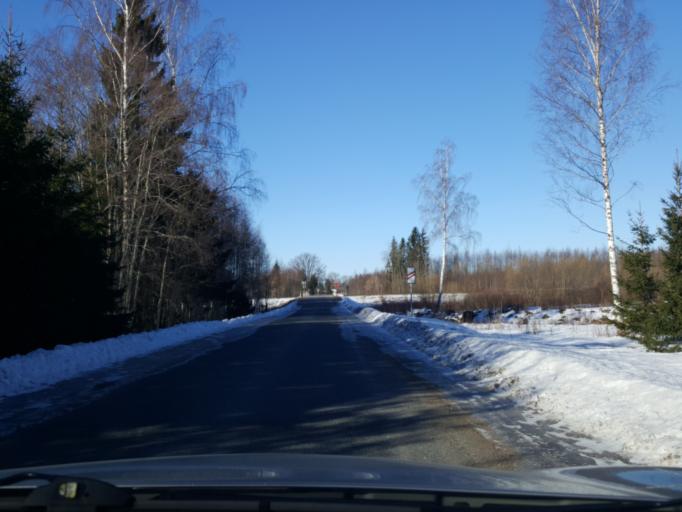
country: EE
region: Viljandimaa
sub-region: Suure-Jaani vald
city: Suure-Jaani
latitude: 58.5368
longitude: 25.5471
